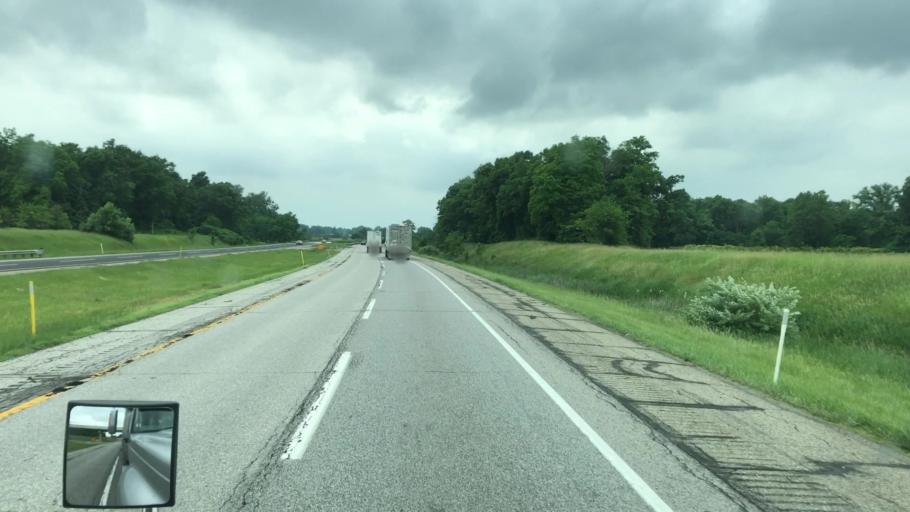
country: US
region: Michigan
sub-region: Branch County
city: Bronson
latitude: 41.7564
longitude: -85.2260
